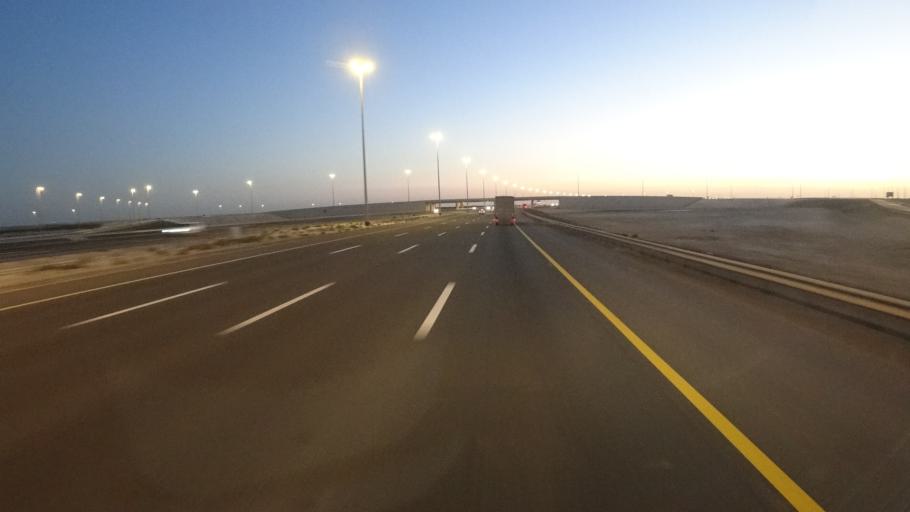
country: AE
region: Dubai
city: Dubai
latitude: 24.7675
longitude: 54.9477
